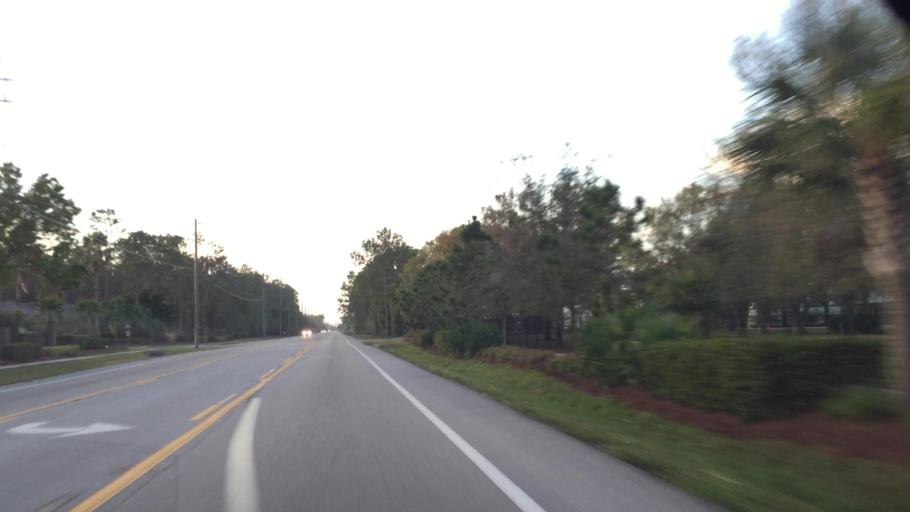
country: US
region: Florida
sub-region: Lee County
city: Pine Manor
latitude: 26.5793
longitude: -81.8473
